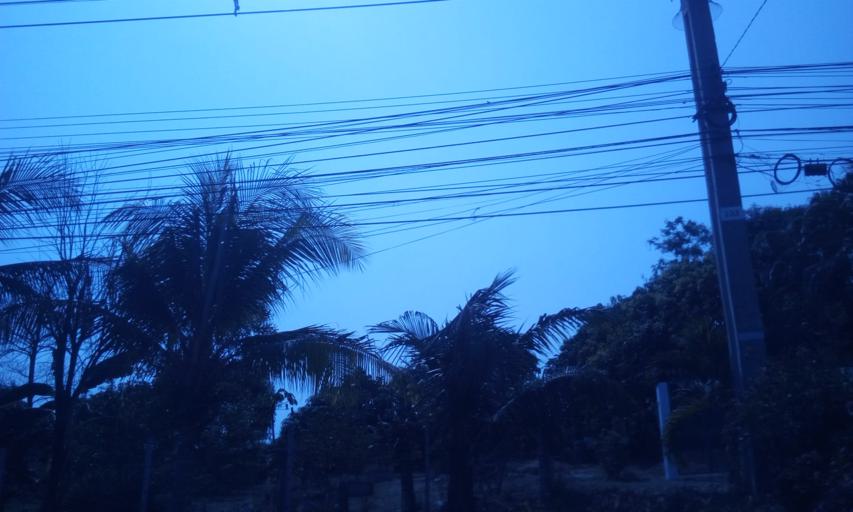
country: TH
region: Nonthaburi
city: Sai Noi
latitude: 14.0373
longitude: 100.3122
